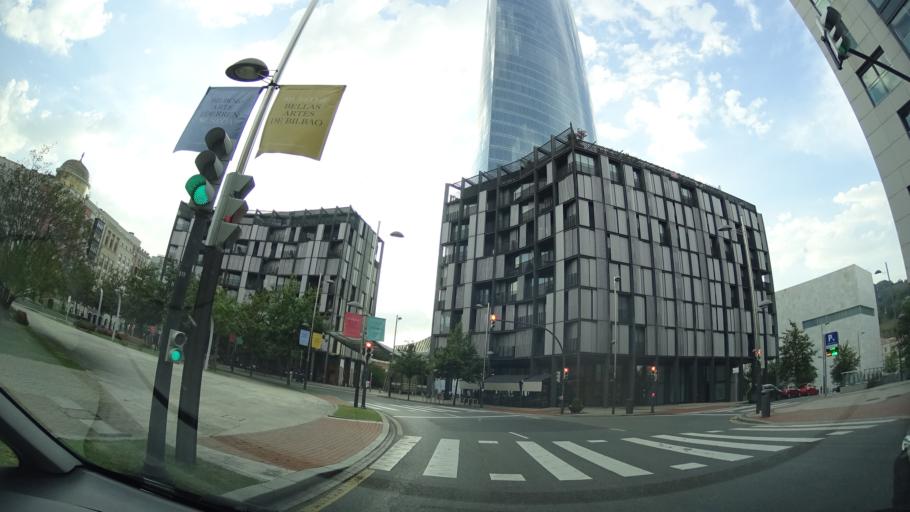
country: ES
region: Basque Country
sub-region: Bizkaia
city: Bilbao
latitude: 43.2673
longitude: -2.9377
